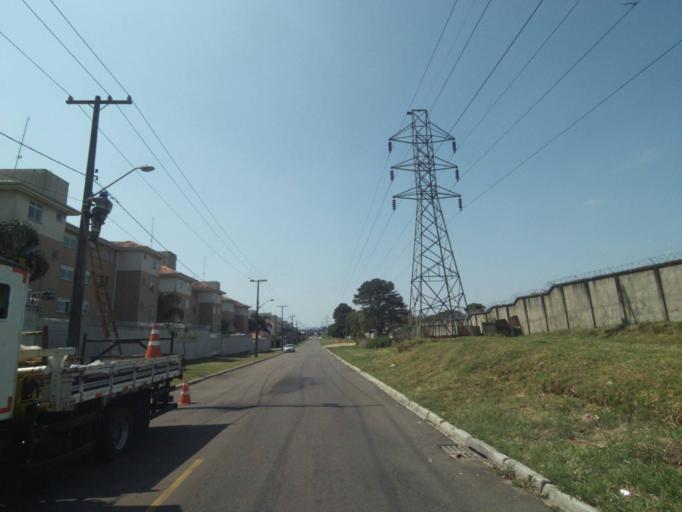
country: BR
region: Parana
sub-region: Curitiba
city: Curitiba
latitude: -25.4876
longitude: -49.3230
